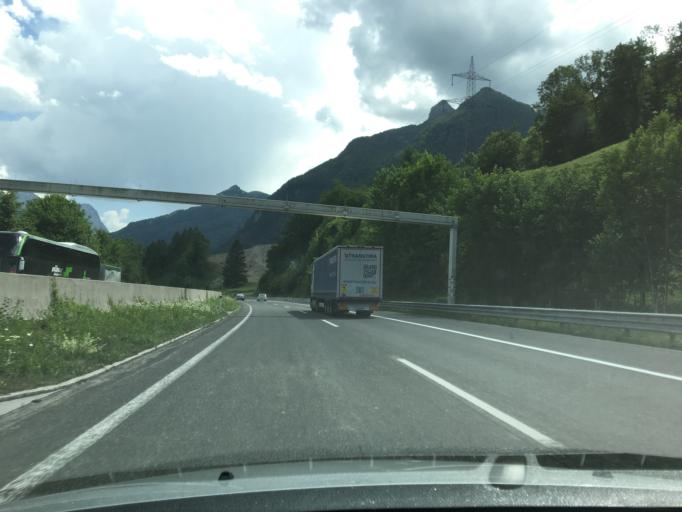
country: AT
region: Salzburg
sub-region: Politischer Bezirk Hallein
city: Kuchl
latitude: 47.6171
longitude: 13.1386
